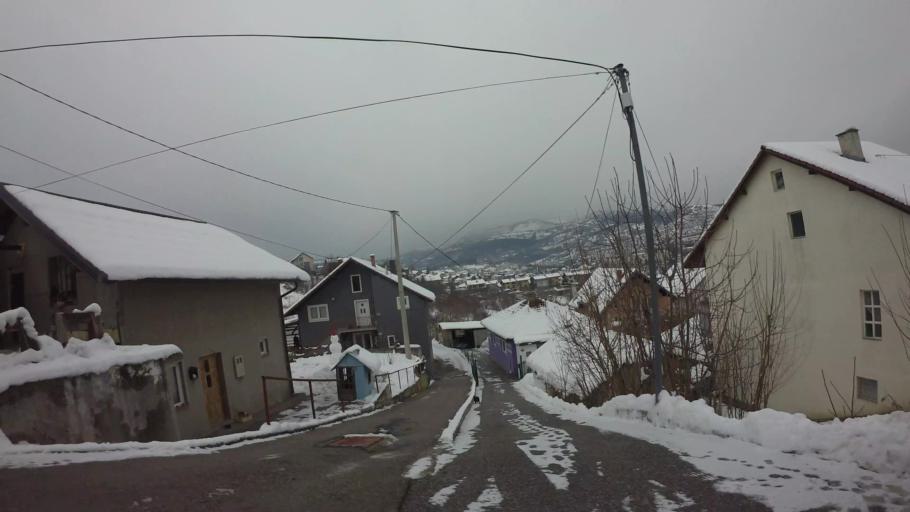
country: BA
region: Federation of Bosnia and Herzegovina
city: Kobilja Glava
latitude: 43.8618
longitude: 18.3956
